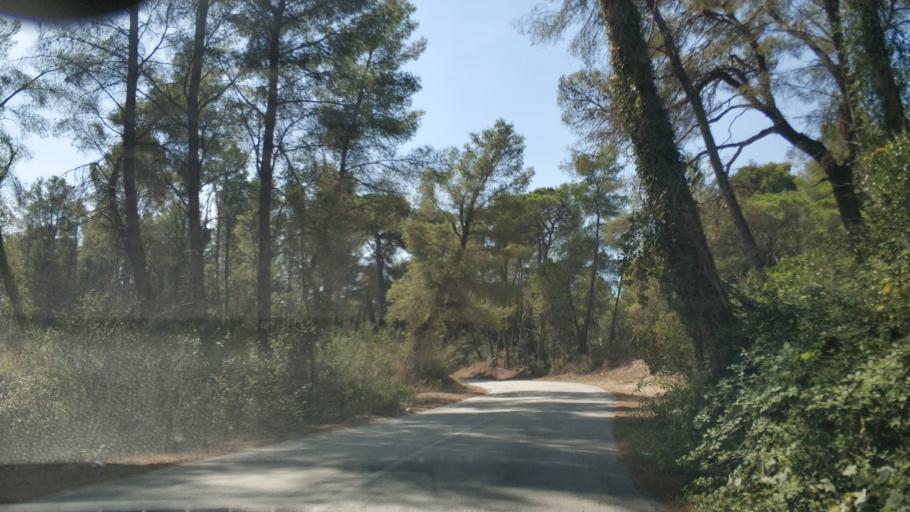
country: AL
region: Fier
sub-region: Rrethi i Lushnjes
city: Divjake
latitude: 40.9870
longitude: 19.4840
